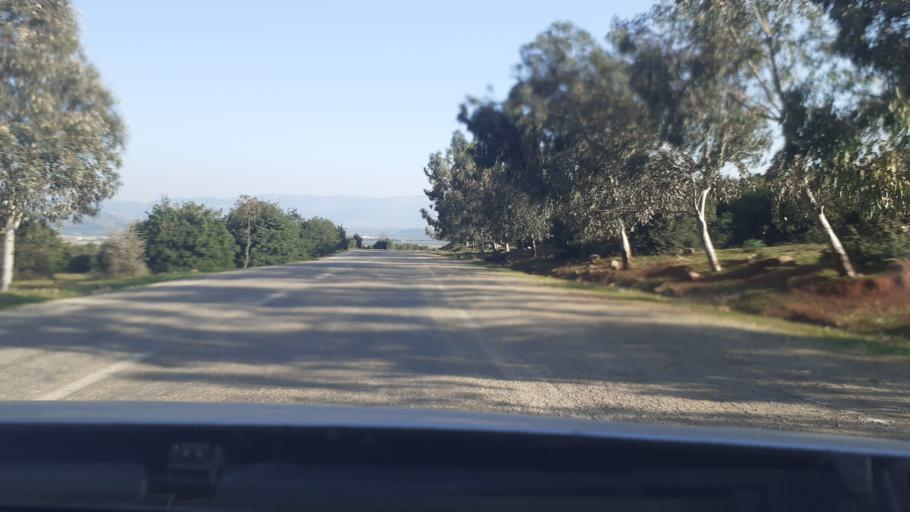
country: TR
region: Hatay
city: Aktepe
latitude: 36.7300
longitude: 36.4812
